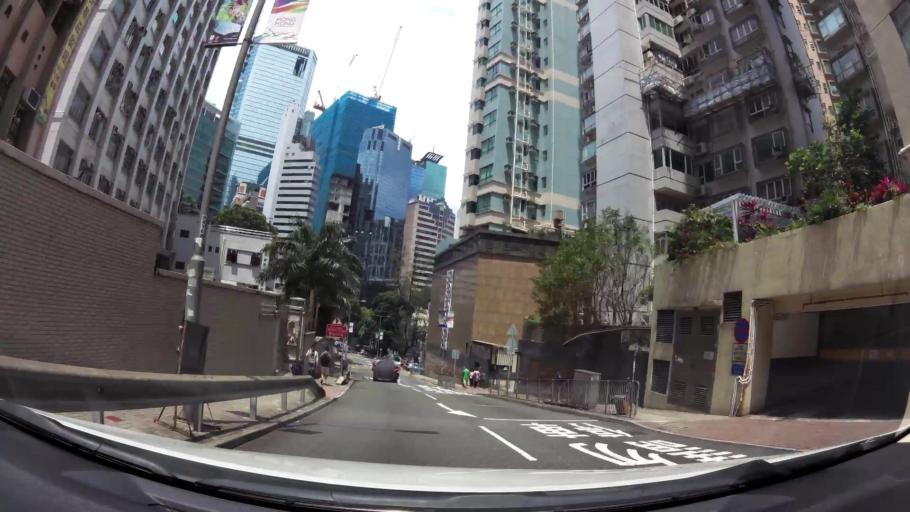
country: HK
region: Wanchai
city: Wan Chai
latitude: 22.2756
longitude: 114.1854
